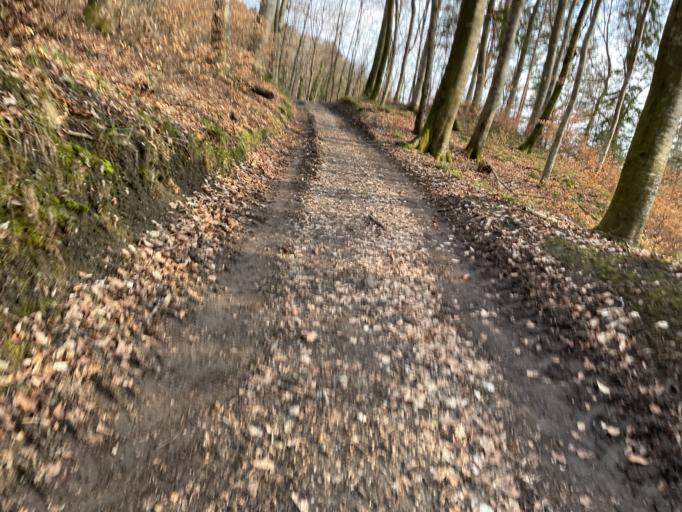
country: CH
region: Bern
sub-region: Bern-Mittelland District
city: Toffen
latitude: 46.8504
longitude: 7.5094
